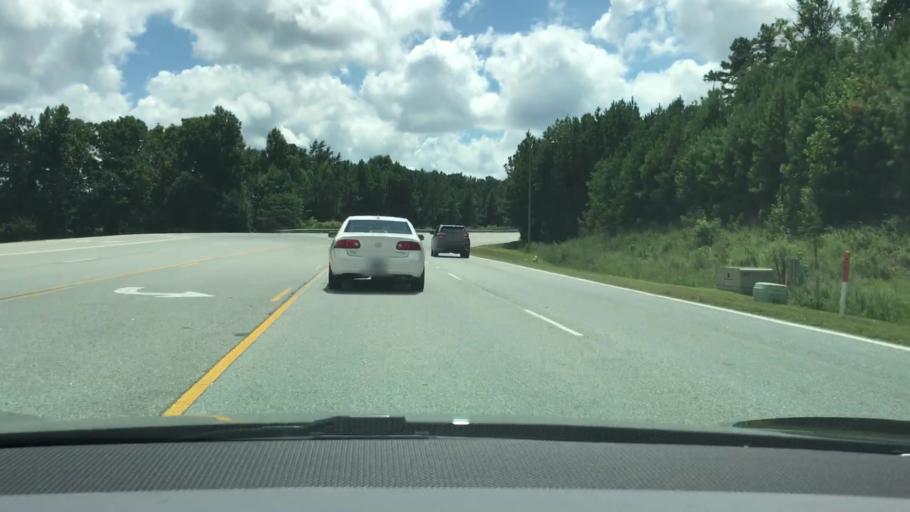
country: US
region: Alabama
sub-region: Lee County
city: Auburn
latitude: 32.6052
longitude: -85.4331
